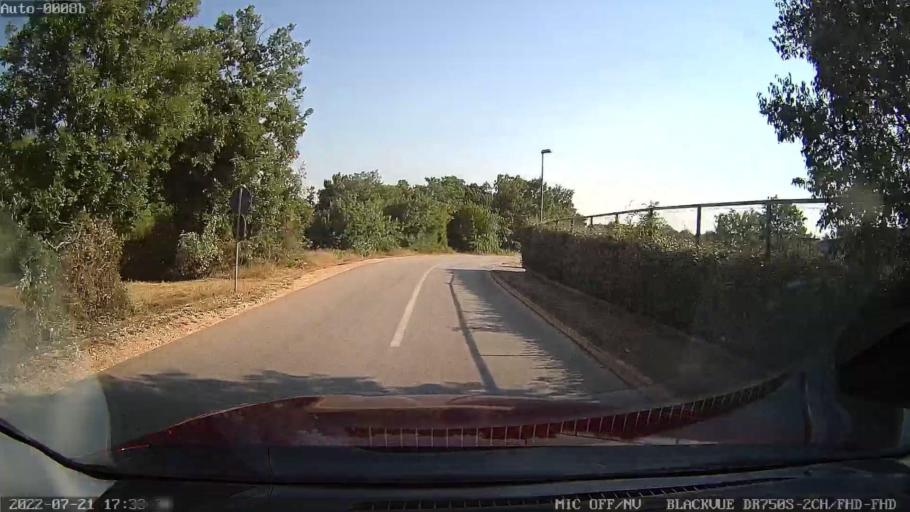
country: HR
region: Istarska
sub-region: Grad Rovinj
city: Rovinj
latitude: 45.1715
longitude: 13.7467
